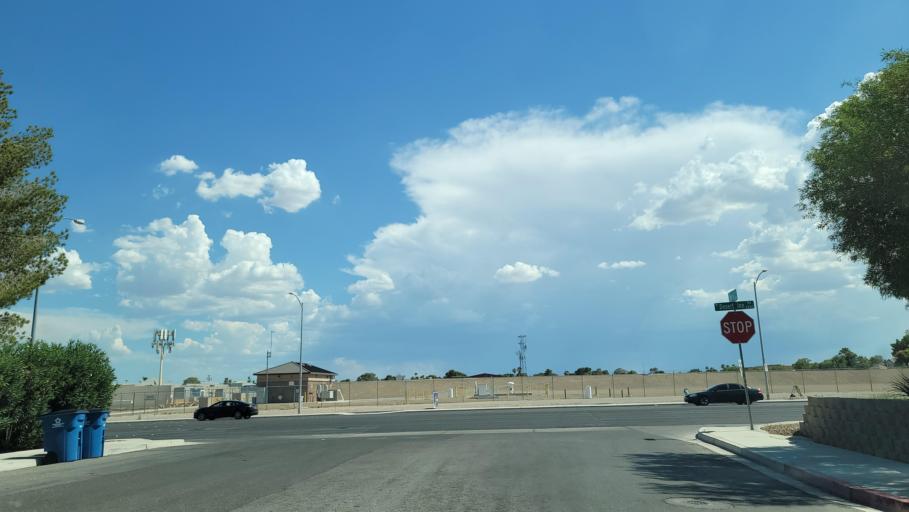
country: US
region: Nevada
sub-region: Clark County
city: Spring Valley
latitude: 36.1296
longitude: -115.2272
